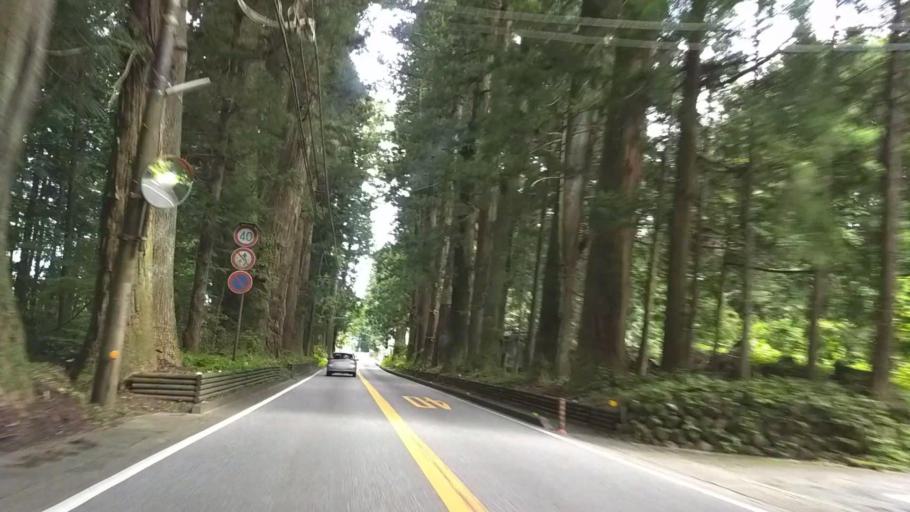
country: JP
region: Tochigi
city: Nikko
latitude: 36.7384
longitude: 139.6388
